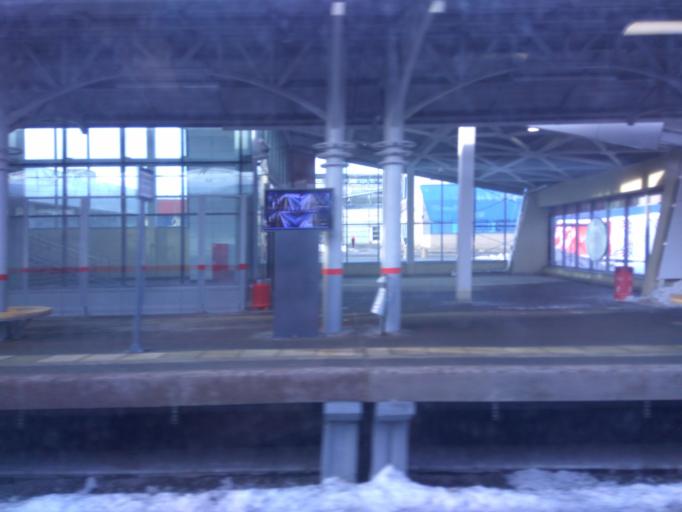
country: RU
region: Moskovskaya
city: Bogorodskoye
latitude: 55.8035
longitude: 37.7459
